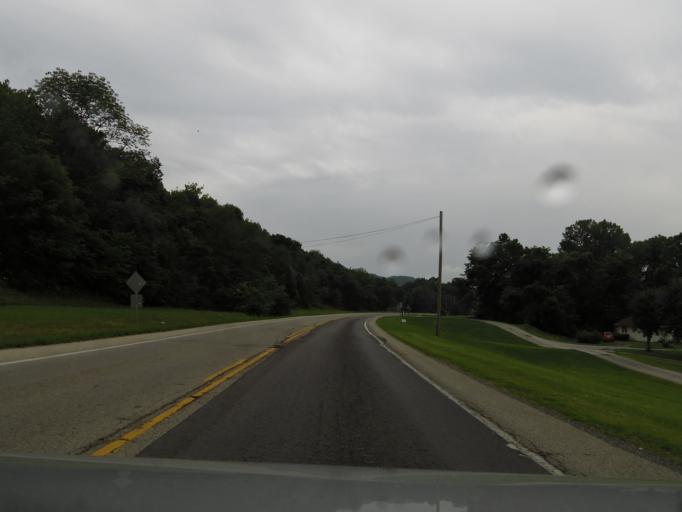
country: US
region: Ohio
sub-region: Brown County
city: Aberdeen
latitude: 38.7012
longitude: -83.7865
